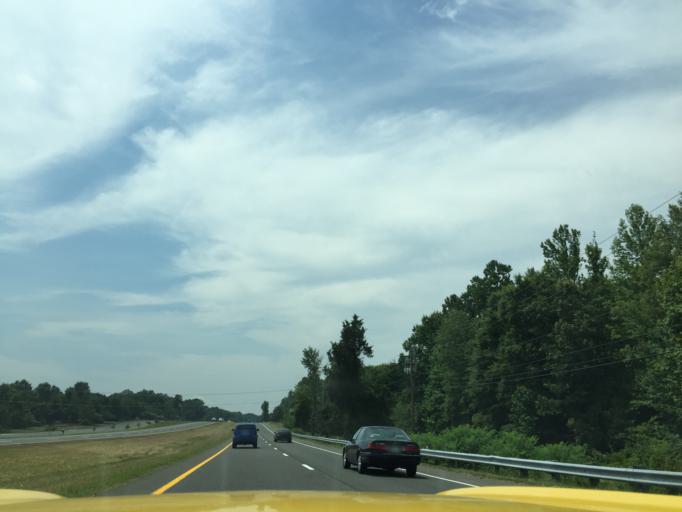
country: US
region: Maryland
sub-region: Prince George's County
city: Accokeek
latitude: 38.6477
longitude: -77.0384
